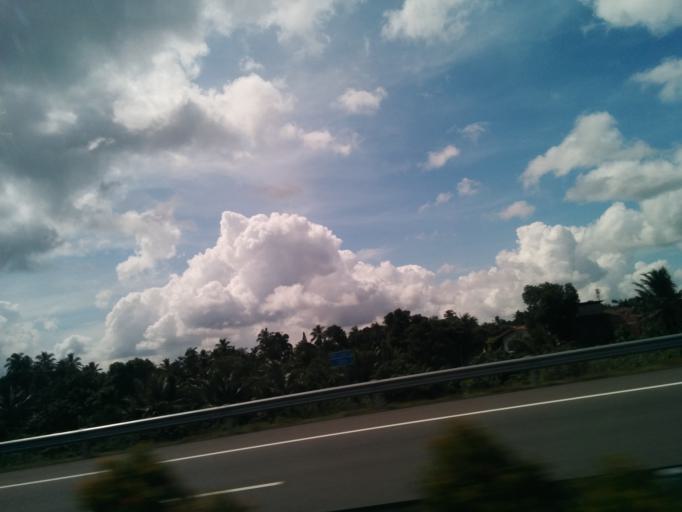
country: LK
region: Western
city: Wattala
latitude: 6.9786
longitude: 79.8988
